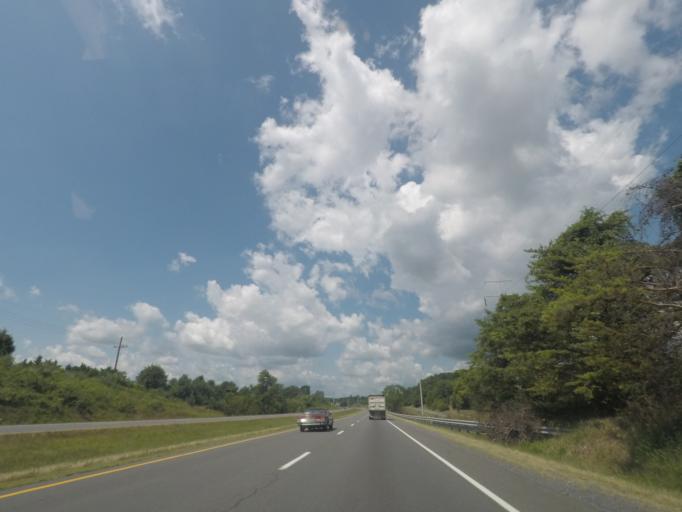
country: US
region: Virginia
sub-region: City of Winchester
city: Winchester
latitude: 39.2131
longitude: -78.1678
